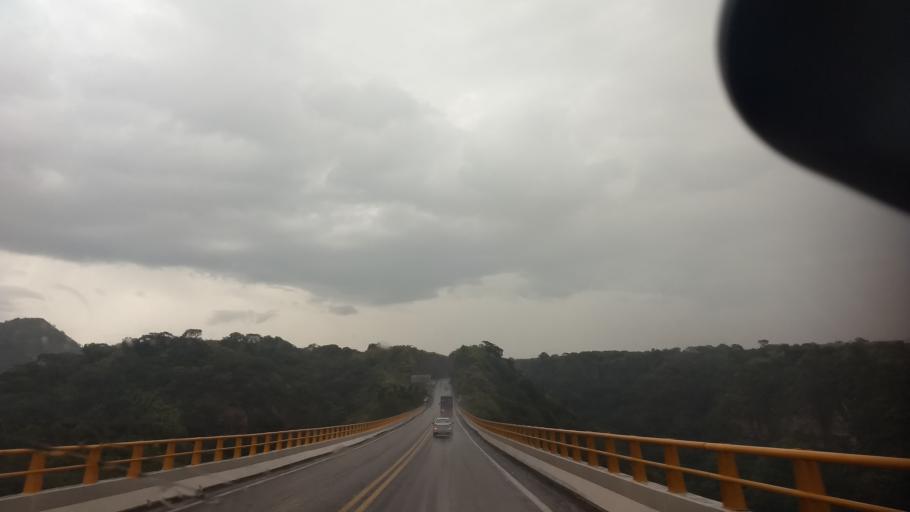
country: MX
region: Jalisco
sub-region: Tonila
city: San Marcos
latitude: 19.4430
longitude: -103.4750
